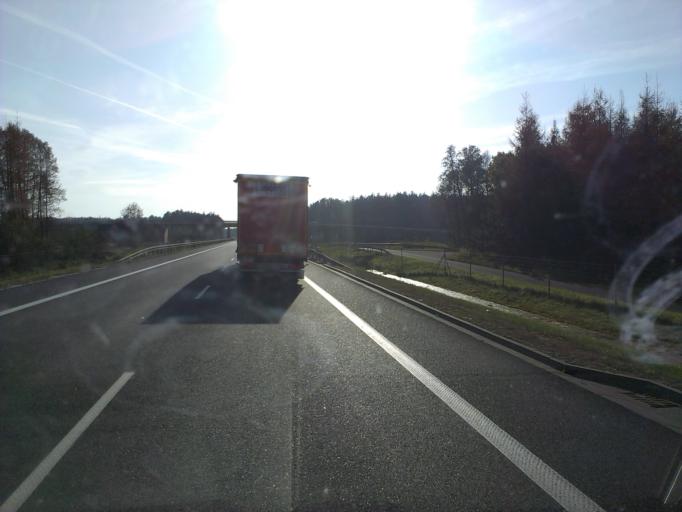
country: PL
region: Lubusz
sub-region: Powiat nowosolski
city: Otyn
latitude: 51.8287
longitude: 15.6753
